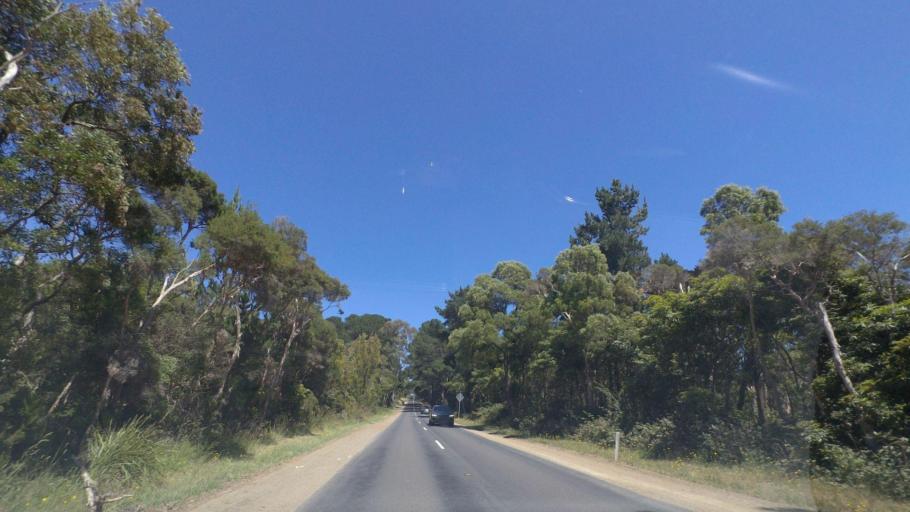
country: AU
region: Victoria
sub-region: Mornington Peninsula
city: Merricks
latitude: -38.3740
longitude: 145.0771
